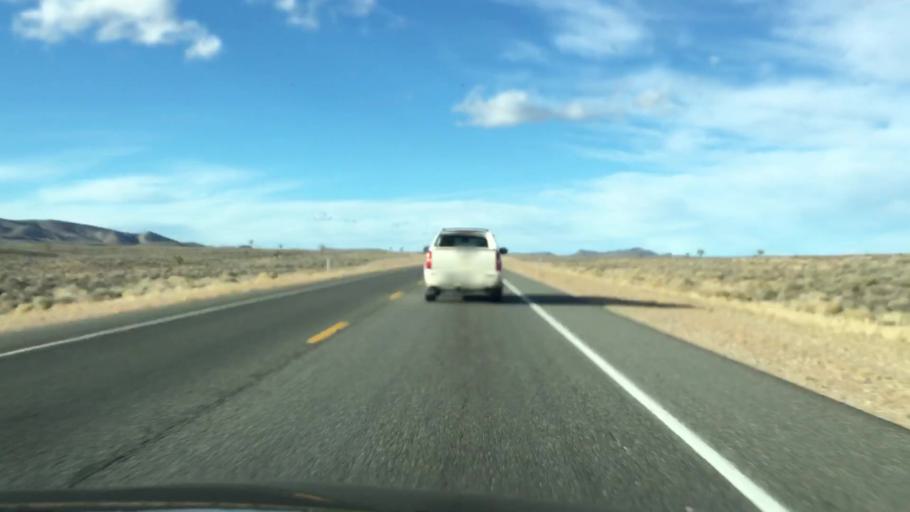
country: US
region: Nevada
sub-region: Esmeralda County
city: Goldfield
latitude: 37.5738
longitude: -117.2025
